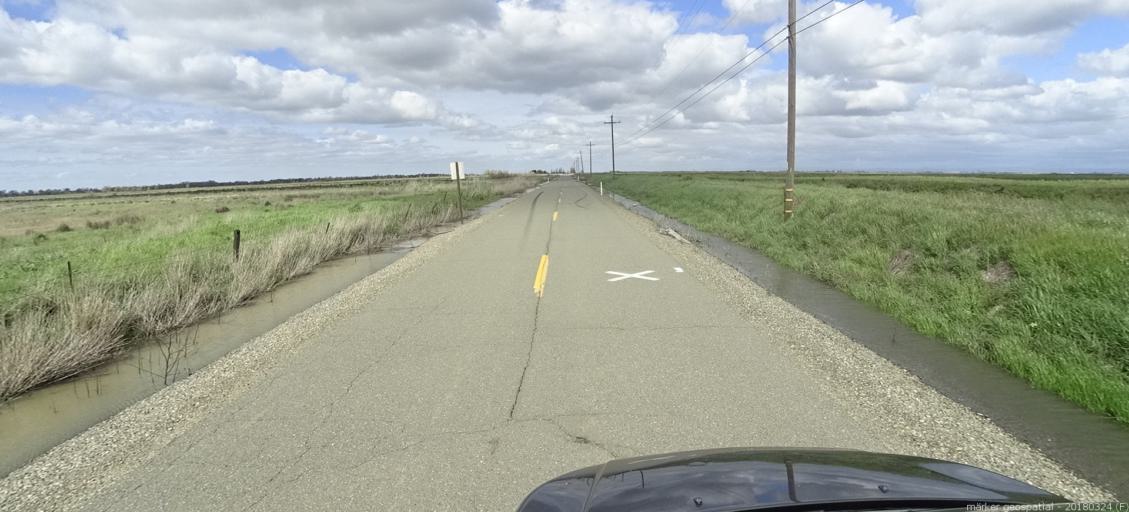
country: US
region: California
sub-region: Sacramento County
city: Elverta
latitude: 38.7209
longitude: -121.5768
